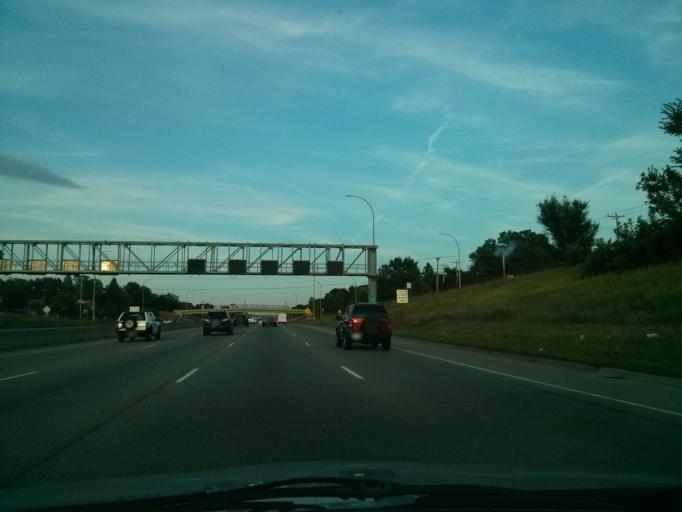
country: US
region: Minnesota
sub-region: Ramsey County
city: Falcon Heights
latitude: 44.9517
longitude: -93.1458
